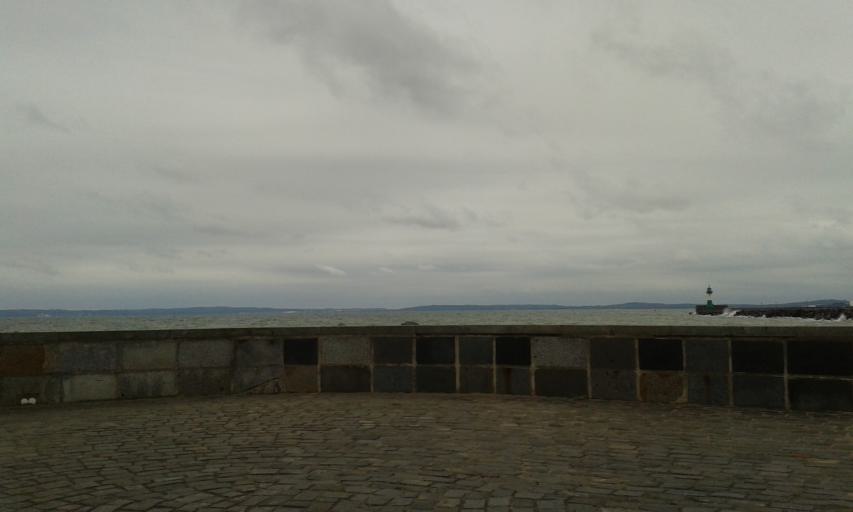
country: DE
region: Mecklenburg-Vorpommern
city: Sassnitz
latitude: 54.5096
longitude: 13.6418
